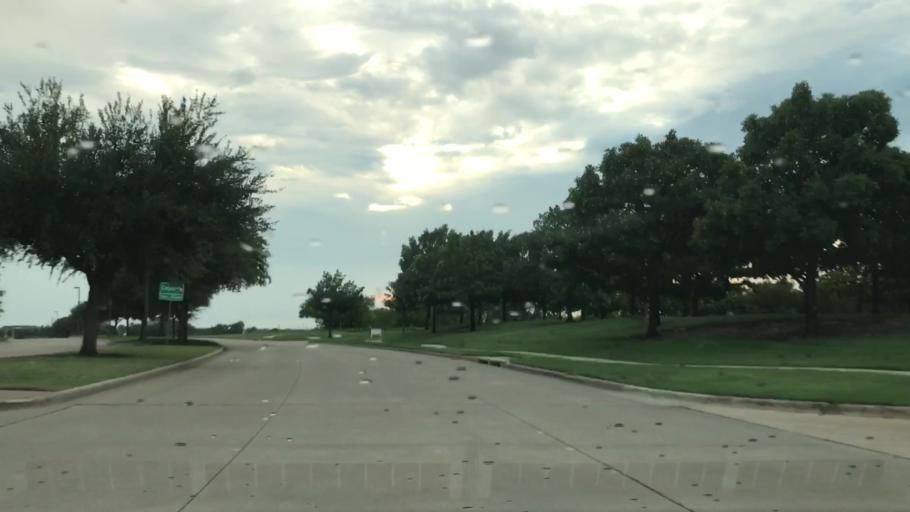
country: US
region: Texas
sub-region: Denton County
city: The Colony
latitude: 33.0721
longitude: -96.8306
